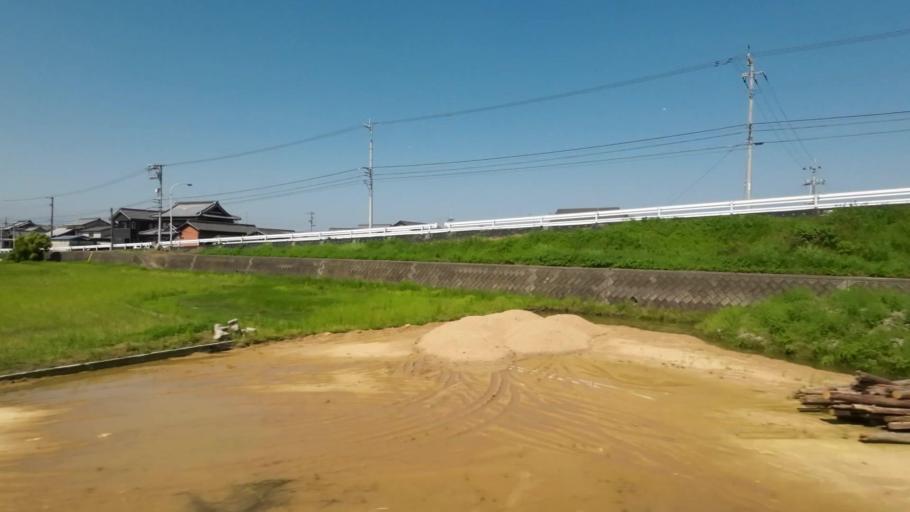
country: JP
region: Kagawa
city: Kan'onjicho
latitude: 34.1087
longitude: 133.6498
